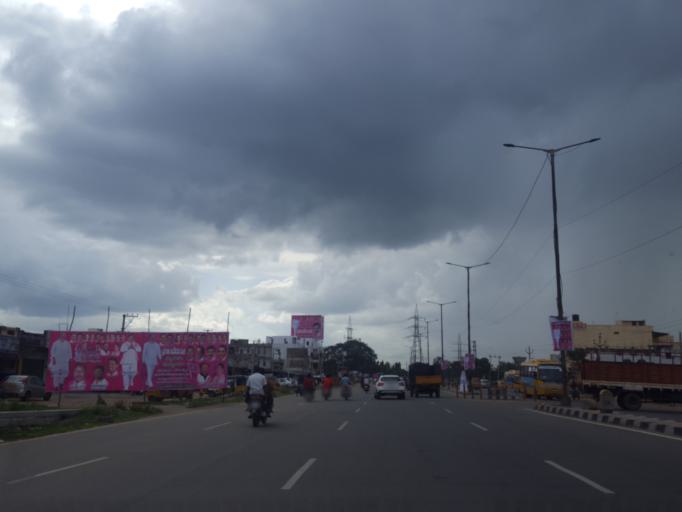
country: IN
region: Telangana
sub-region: Medak
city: Serilingampalle
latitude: 17.5140
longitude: 78.2869
